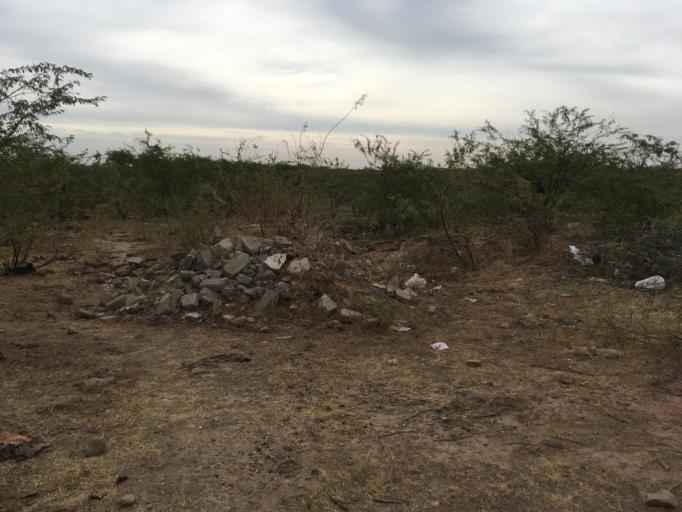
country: IN
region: Gujarat
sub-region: Kachchh
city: Bhuj
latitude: 23.2516
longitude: 69.6298
